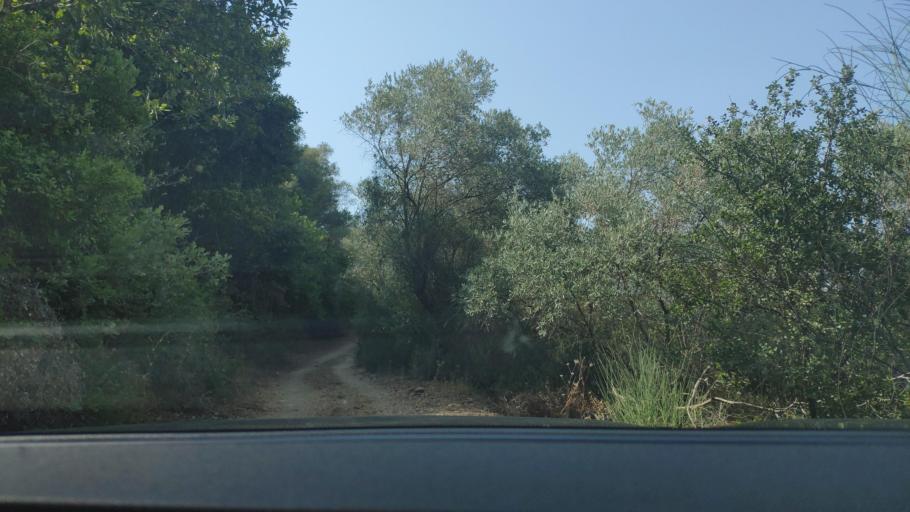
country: GR
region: West Greece
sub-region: Nomos Aitolias kai Akarnanias
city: Fitiai
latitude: 38.7330
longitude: 21.1828
